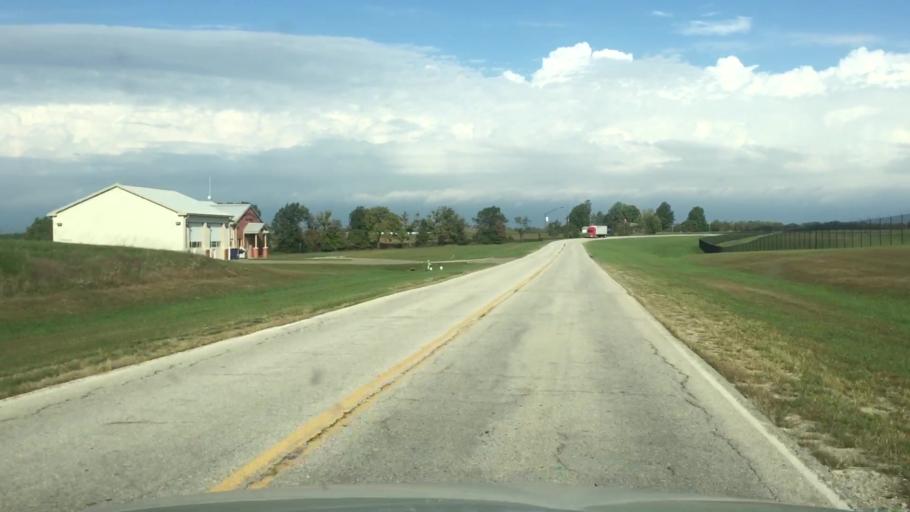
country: US
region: Missouri
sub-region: Boone County
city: Ashland
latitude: 38.8247
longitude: -92.2239
